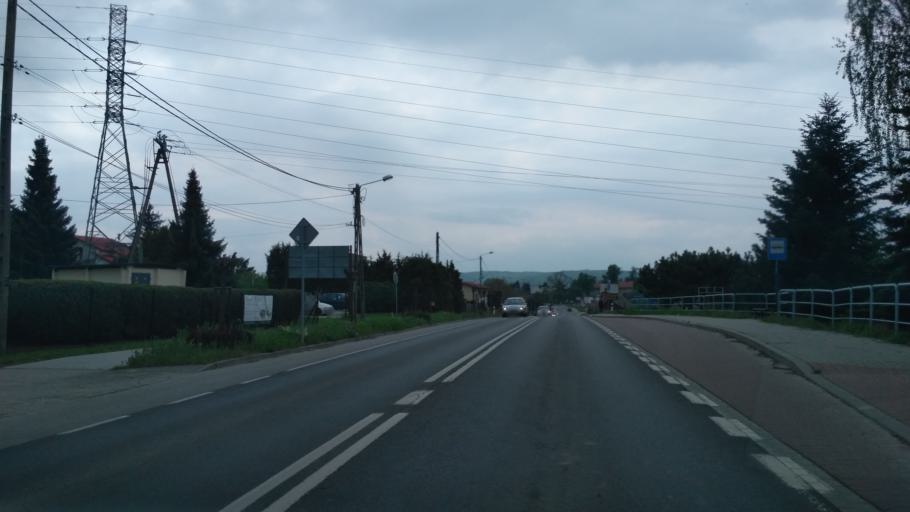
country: PL
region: Lesser Poland Voivodeship
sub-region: Powiat tarnowski
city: Tarnowiec
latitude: 49.9883
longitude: 20.9853
